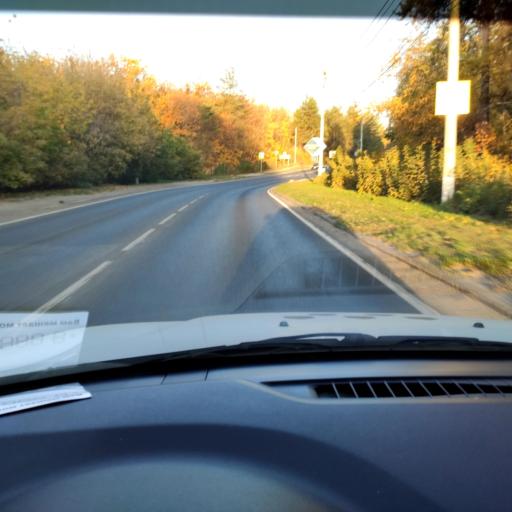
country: RU
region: Samara
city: Tol'yatti
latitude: 53.4939
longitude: 49.2933
